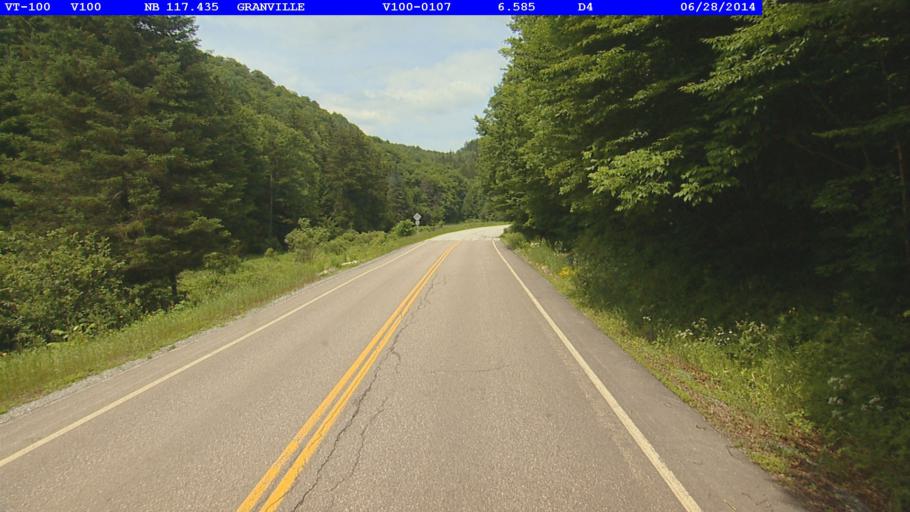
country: US
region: Vermont
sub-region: Orange County
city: Randolph
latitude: 44.0257
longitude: -72.8343
